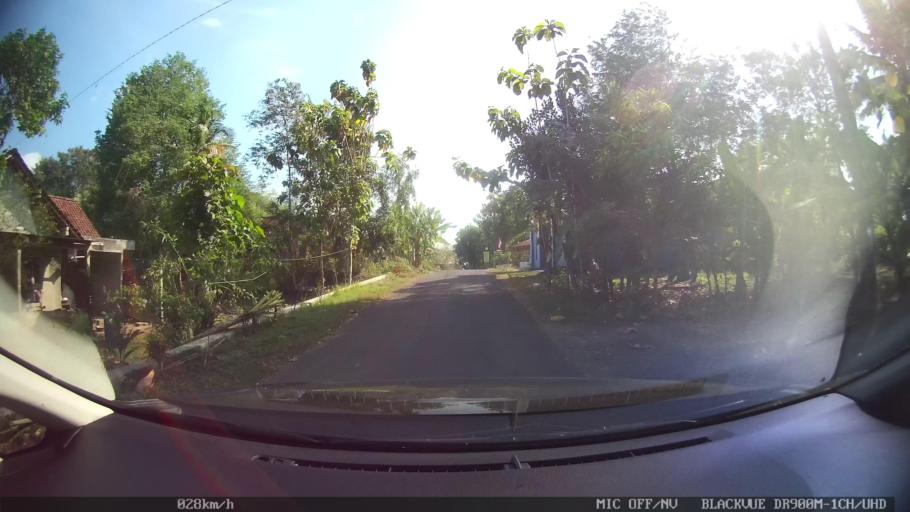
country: ID
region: Daerah Istimewa Yogyakarta
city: Kasihan
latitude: -7.8329
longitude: 110.2874
